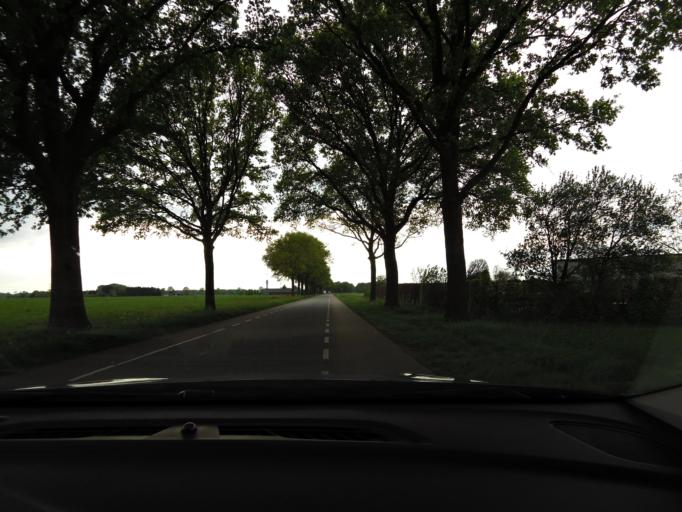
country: NL
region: North Brabant
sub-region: Gemeente Loon op Zand
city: Loon op Zand
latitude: 51.6107
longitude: 5.1066
